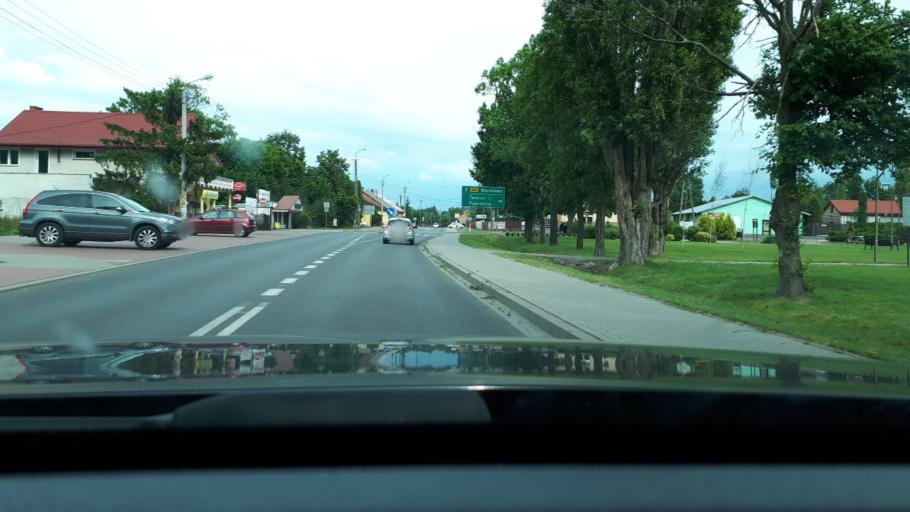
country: PL
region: Masovian Voivodeship
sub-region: Powiat warszawski zachodni
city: Kampinos
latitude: 52.2683
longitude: 20.4617
